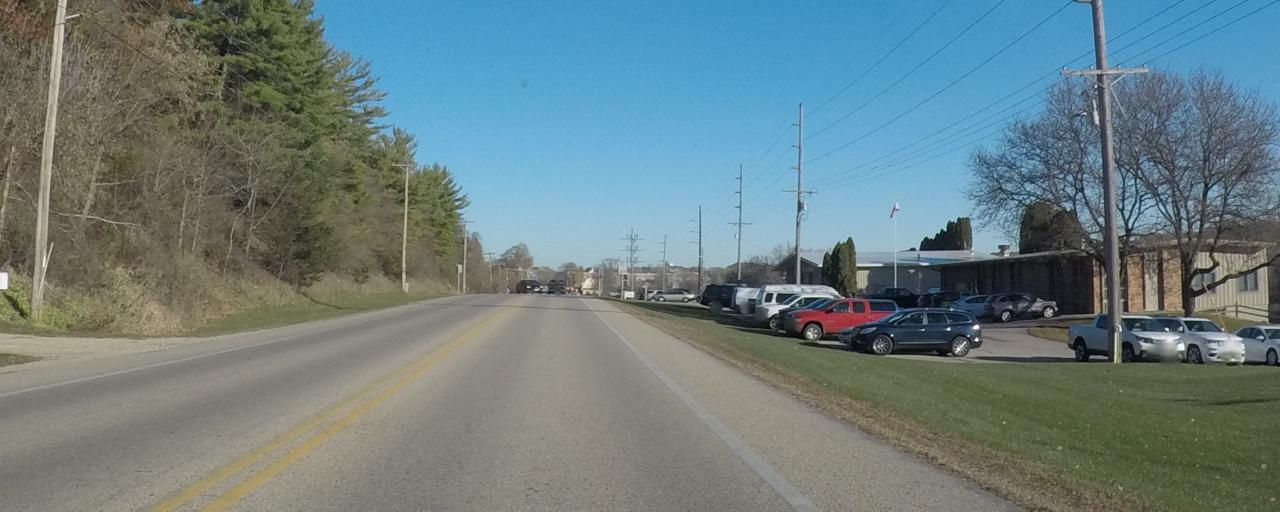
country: US
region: Wisconsin
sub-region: Dane County
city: Cottage Grove
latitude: 43.0696
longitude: -89.1997
